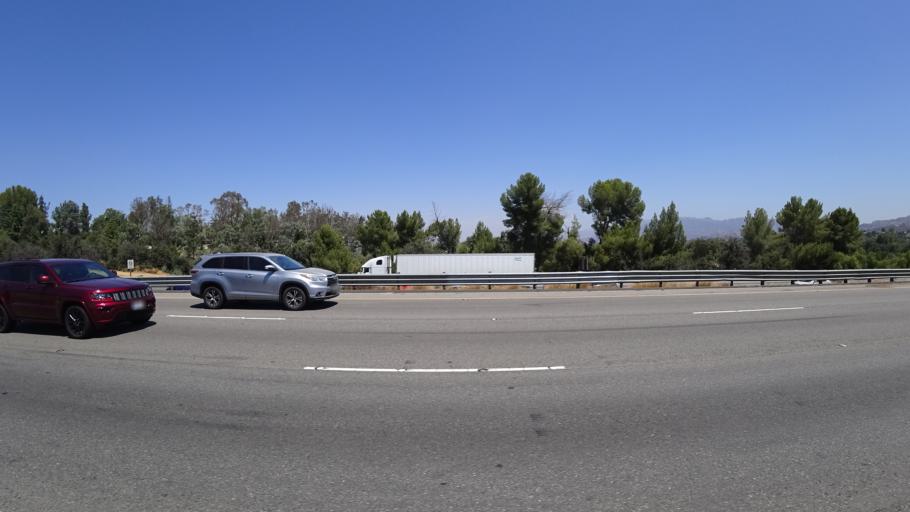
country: US
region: California
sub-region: Los Angeles County
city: Santa Clarita
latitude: 34.3899
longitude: -118.5705
